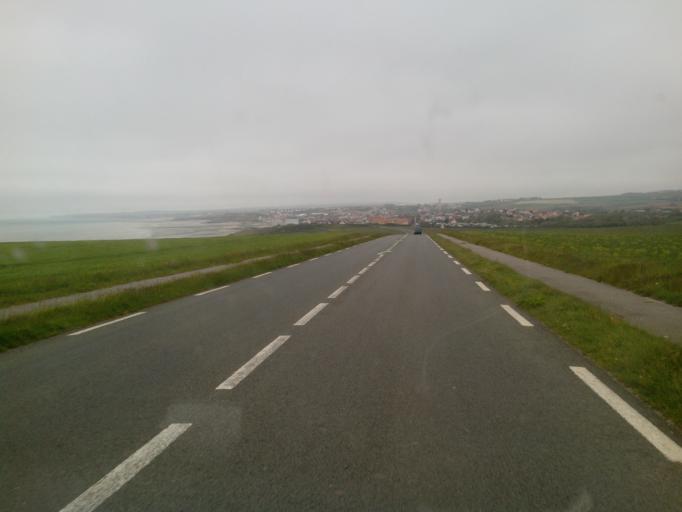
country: FR
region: Nord-Pas-de-Calais
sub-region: Departement du Pas-de-Calais
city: Wimereux
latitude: 50.7527
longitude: 1.6022
